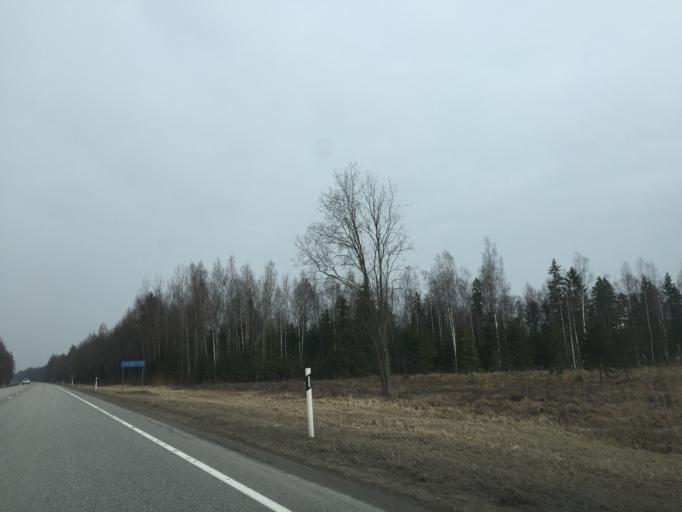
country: LV
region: Salacgrivas
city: Ainazi
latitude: 58.0515
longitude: 24.5106
